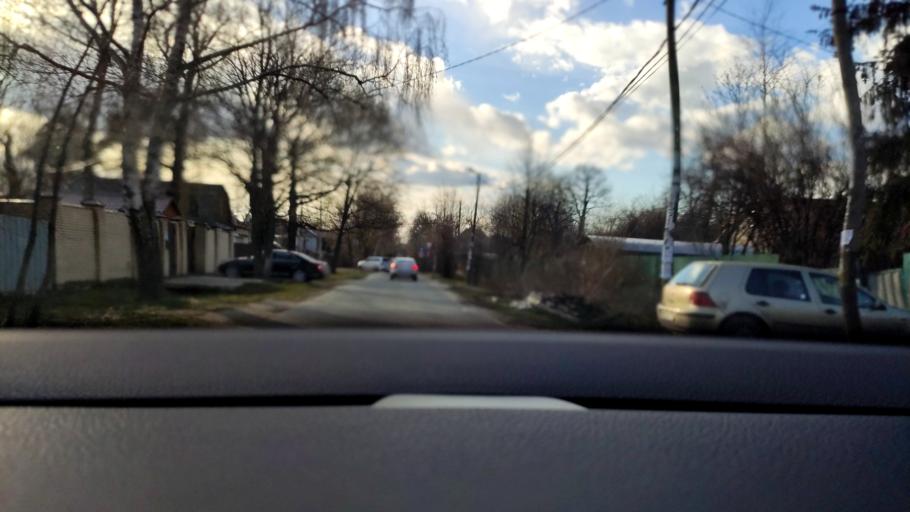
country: RU
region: Moskovskaya
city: Reutov
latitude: 55.7719
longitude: 37.8914
